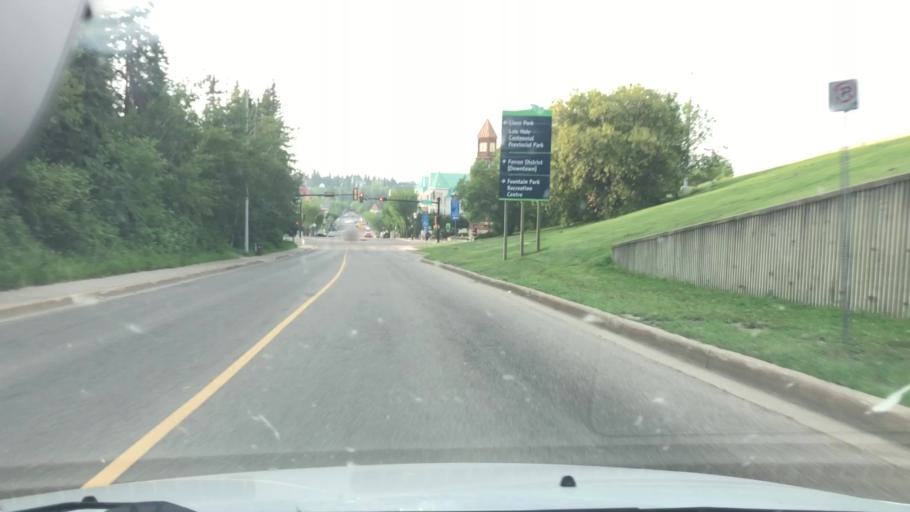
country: CA
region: Alberta
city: St. Albert
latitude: 53.6309
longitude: -113.6224
